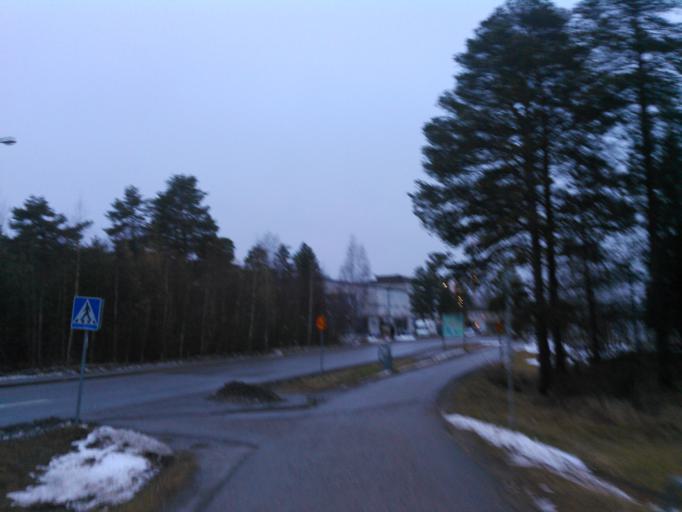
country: SE
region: Vaesterbotten
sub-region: Umea Kommun
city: Umea
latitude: 63.8141
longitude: 20.3035
